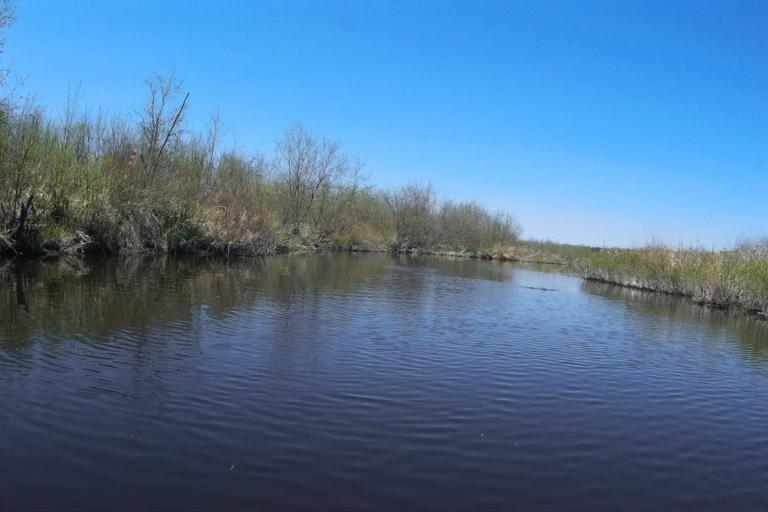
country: CA
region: Ontario
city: Powassan
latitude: 46.1549
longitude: -79.2448
